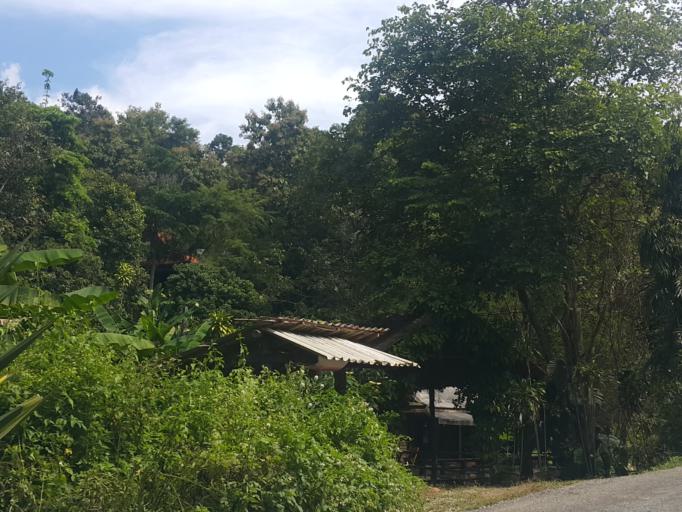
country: TH
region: Chiang Mai
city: Mae On
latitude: 18.8632
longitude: 99.2995
